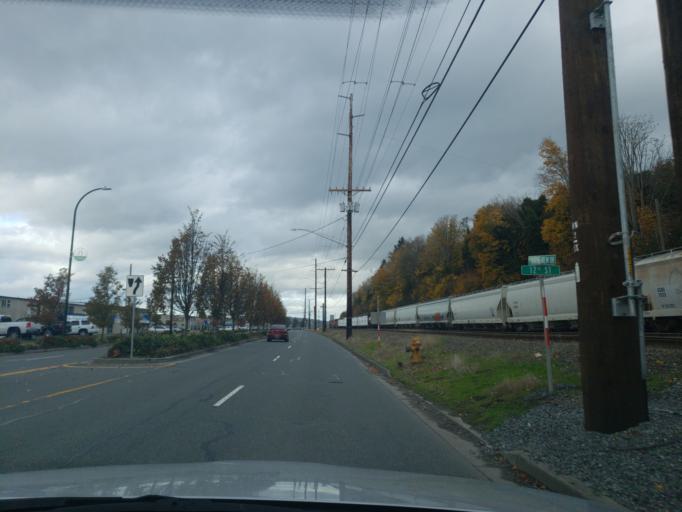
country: US
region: Washington
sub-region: Snohomish County
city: Everett
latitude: 48.0018
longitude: -122.2138
